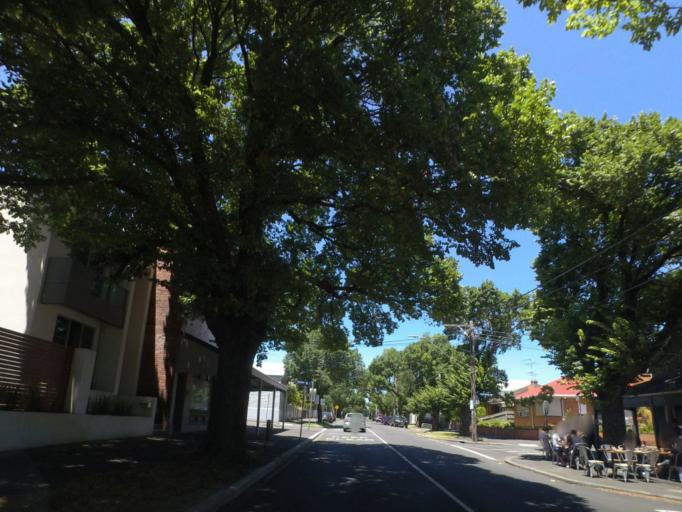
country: AU
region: Victoria
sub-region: Moonee Valley
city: Flemington
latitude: -37.7919
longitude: 144.9257
